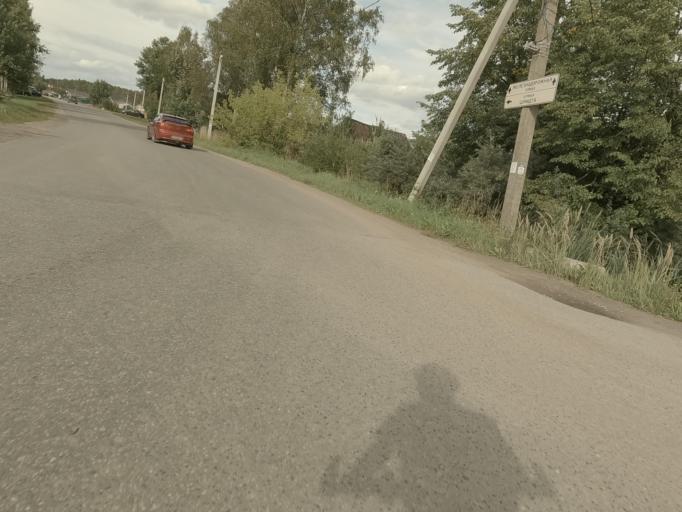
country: RU
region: Leningrad
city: Mga
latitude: 59.7553
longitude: 31.0760
